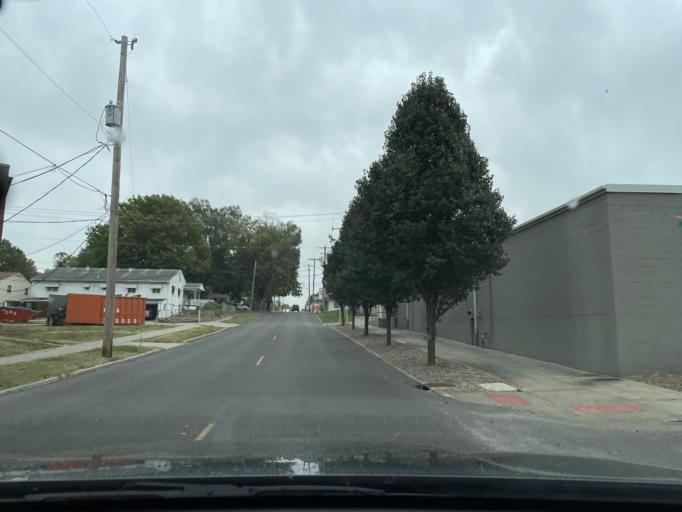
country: US
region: Missouri
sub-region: Buchanan County
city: Saint Joseph
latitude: 39.7768
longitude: -94.8330
